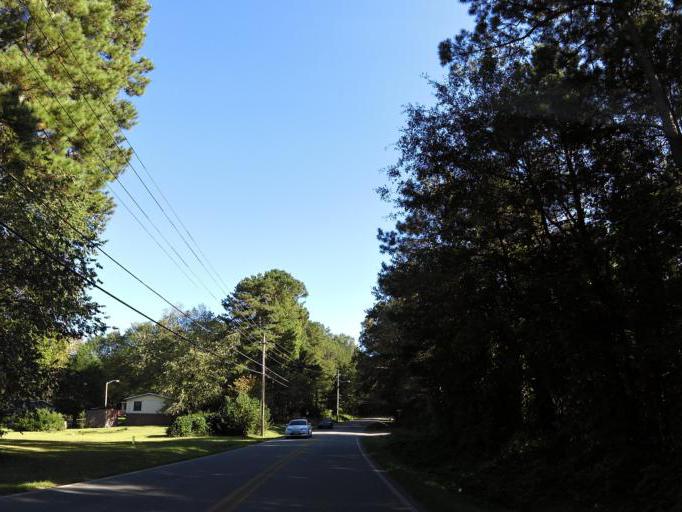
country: US
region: Georgia
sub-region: Cobb County
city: Acworth
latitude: 34.1268
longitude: -84.6811
